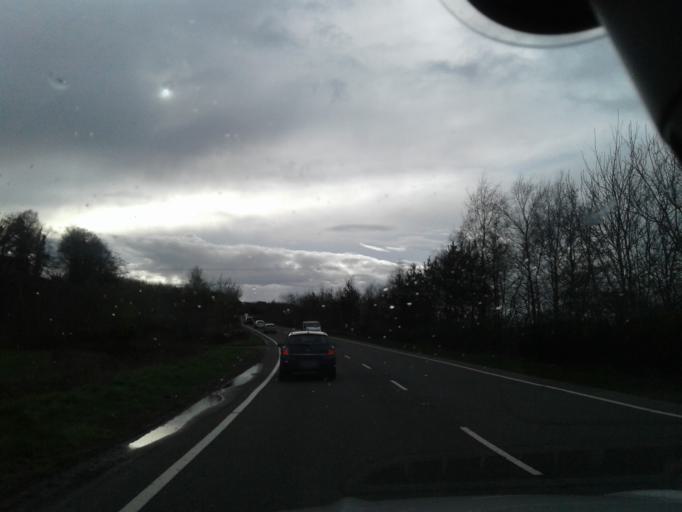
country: GB
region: Northern Ireland
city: Newtownstewart
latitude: 54.7234
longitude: -7.3861
